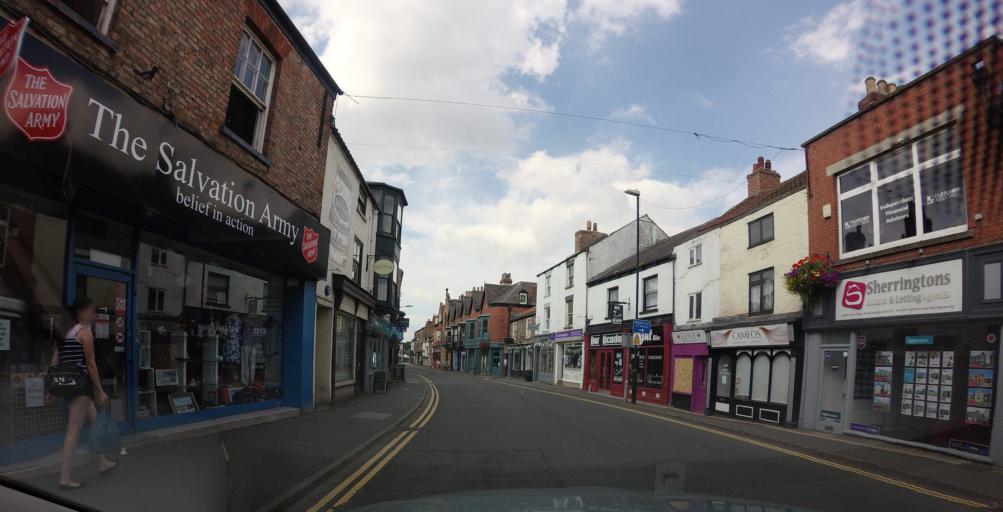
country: GB
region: England
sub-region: North Yorkshire
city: Ripon
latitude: 54.1376
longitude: -1.5236
